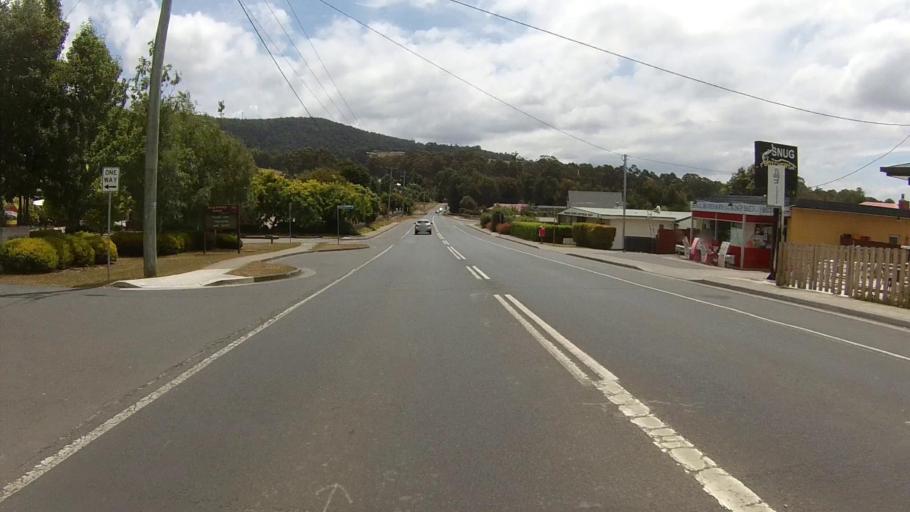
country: AU
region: Tasmania
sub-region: Kingborough
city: Margate
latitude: -43.0661
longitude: 147.2551
